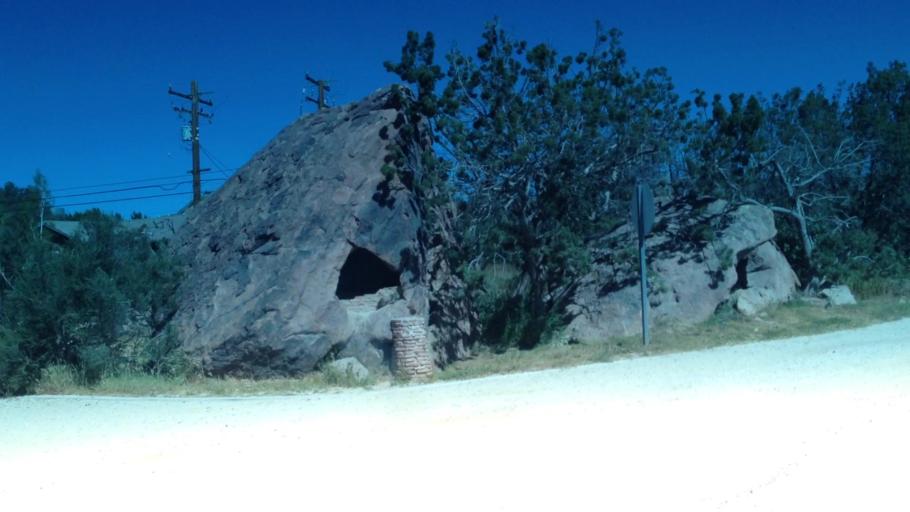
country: US
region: California
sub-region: Los Angeles County
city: Agua Dulce
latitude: 34.4887
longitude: -118.3207
